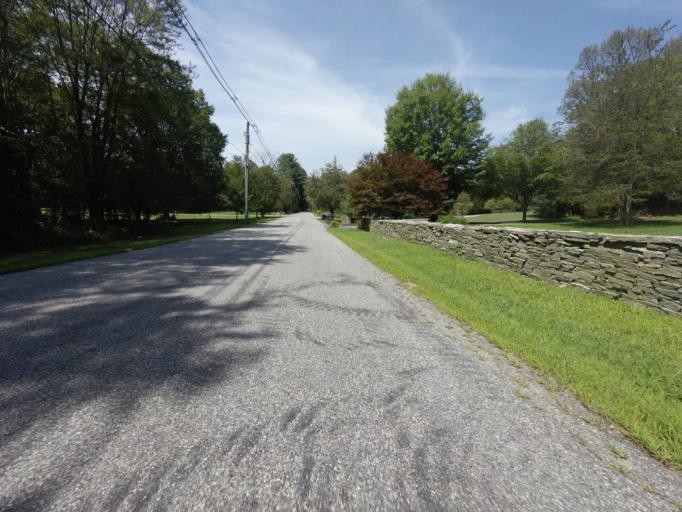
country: US
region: Connecticut
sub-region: Windham County
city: East Brooklyn
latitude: 41.8245
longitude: -71.9311
